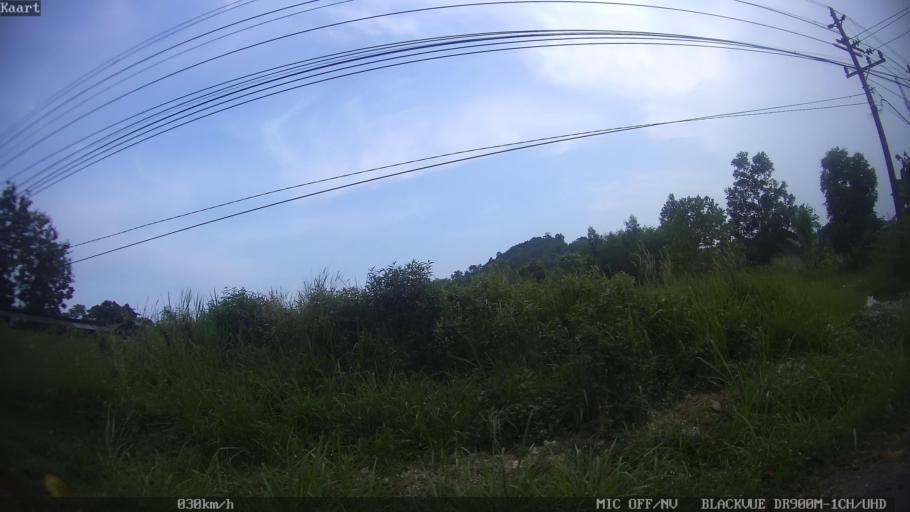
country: ID
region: Lampung
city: Panjang
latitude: -5.4180
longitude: 105.3287
